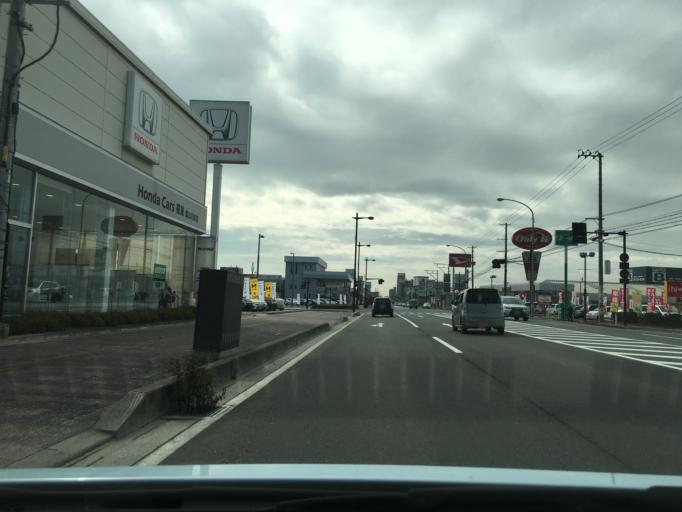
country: JP
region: Fukushima
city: Koriyama
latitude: 37.3720
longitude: 140.3724
